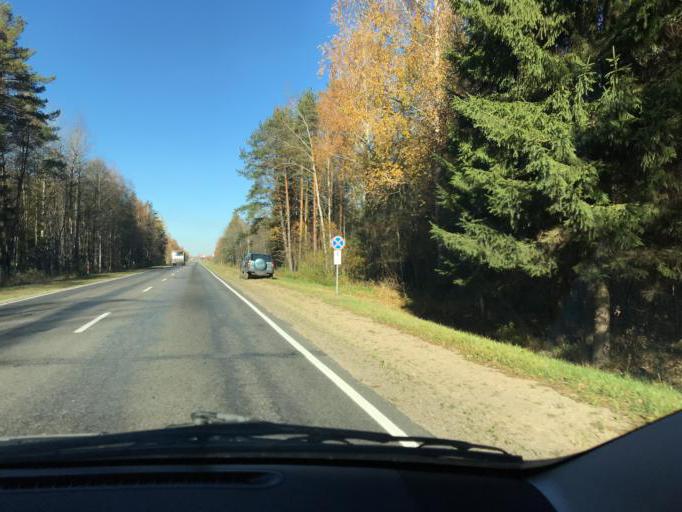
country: BY
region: Vitebsk
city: Polatsk
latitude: 55.4423
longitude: 28.7751
